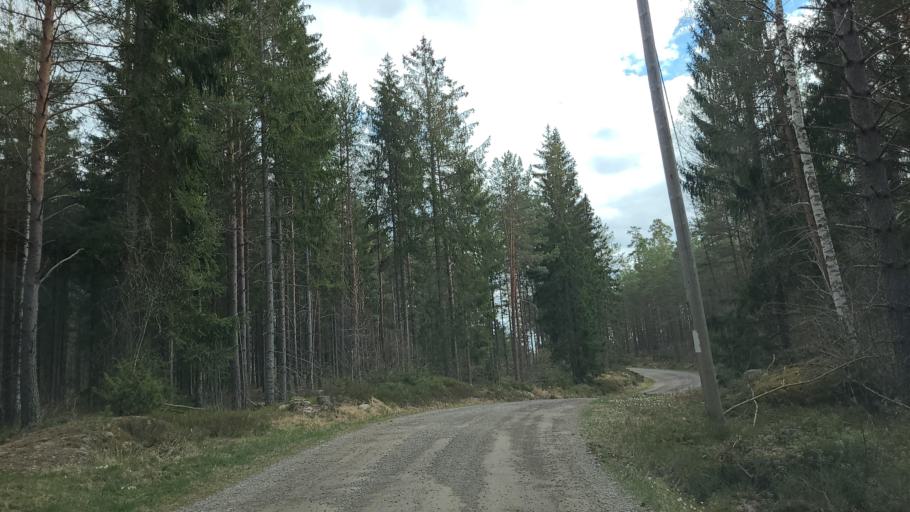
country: SE
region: OEstergoetland
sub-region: Norrkopings Kommun
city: Krokek
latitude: 58.6835
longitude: 16.4230
